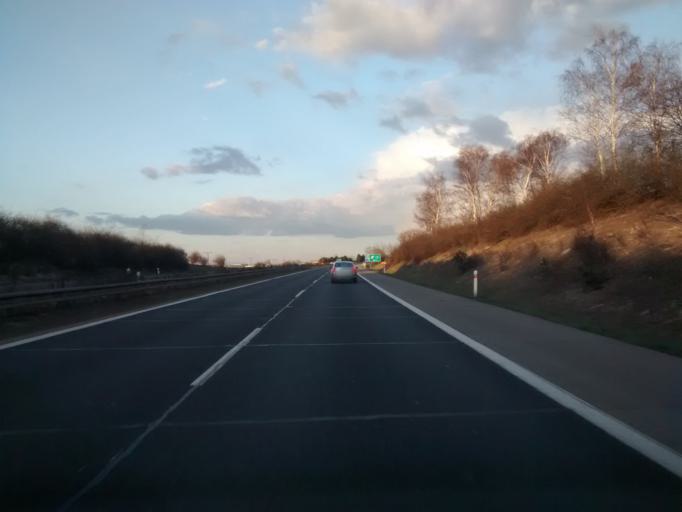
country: CZ
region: Central Bohemia
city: Prerov nad Labem
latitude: 50.1362
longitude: 14.8261
